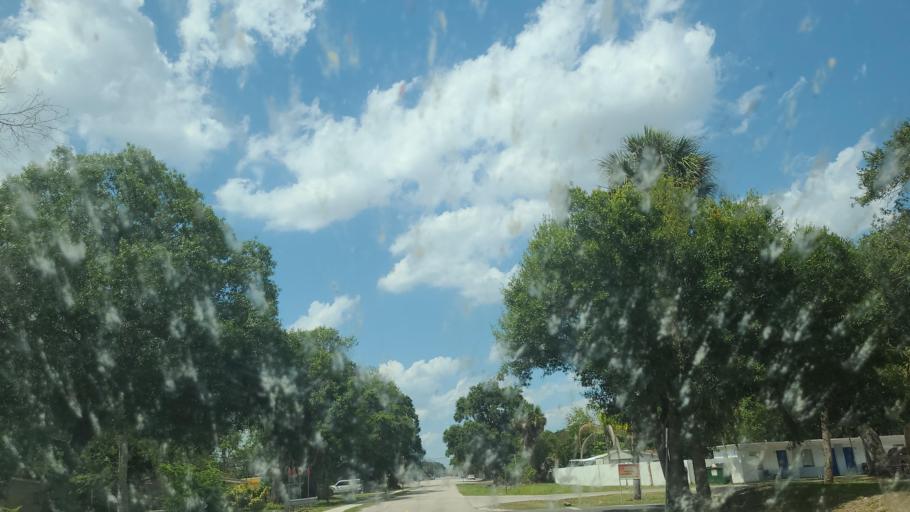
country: US
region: Florida
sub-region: Okeechobee County
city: Okeechobee
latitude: 27.2327
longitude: -80.8311
